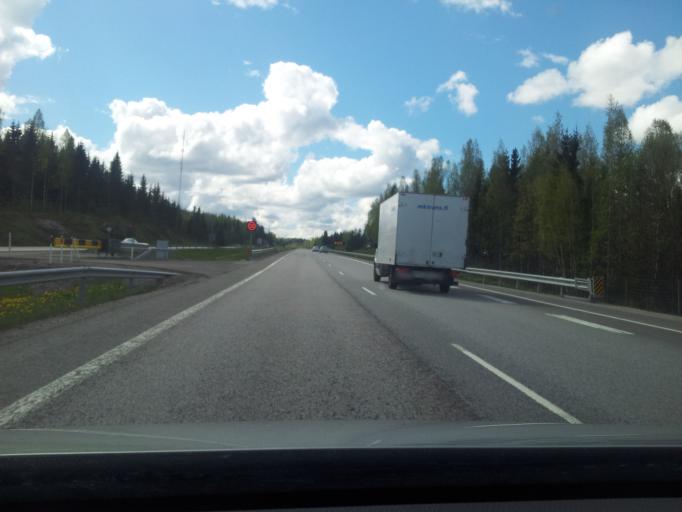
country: FI
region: Uusimaa
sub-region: Loviisa
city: Perna
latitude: 60.4835
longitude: 25.8839
